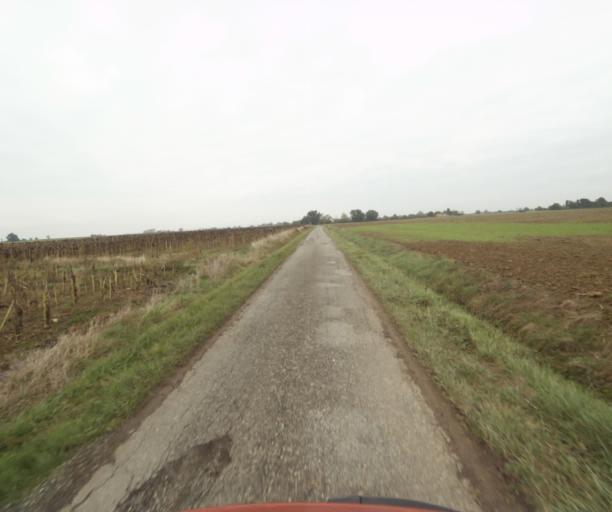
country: FR
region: Midi-Pyrenees
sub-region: Departement de la Haute-Garonne
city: Launac
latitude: 43.8052
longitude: 1.1858
